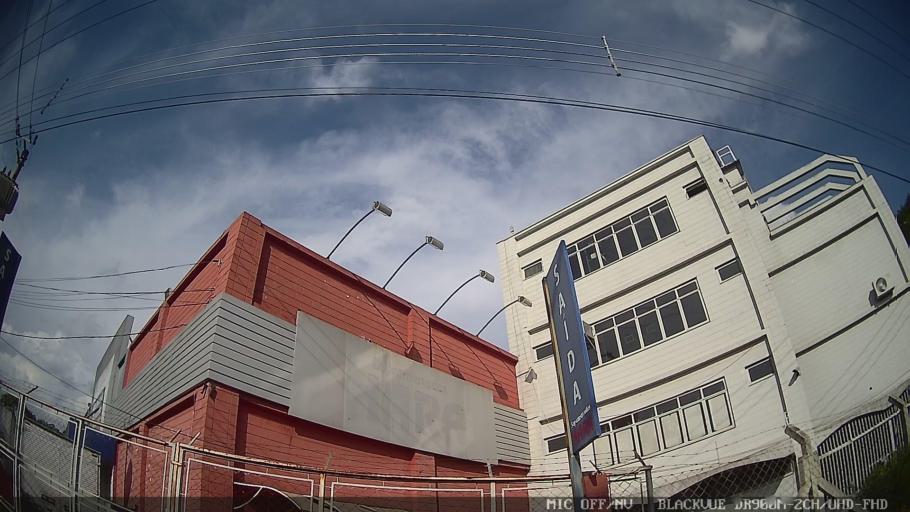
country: BR
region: Sao Paulo
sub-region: Braganca Paulista
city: Braganca Paulista
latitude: -22.9382
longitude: -46.5360
